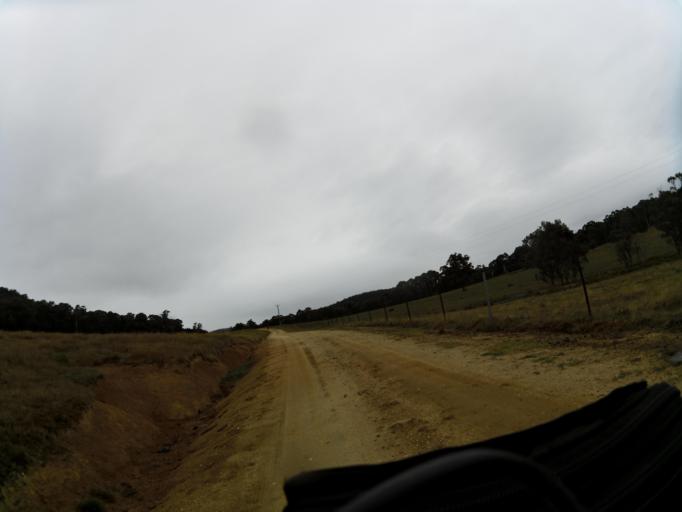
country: AU
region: New South Wales
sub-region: Greater Hume Shire
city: Holbrook
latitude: -36.1637
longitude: 147.4949
